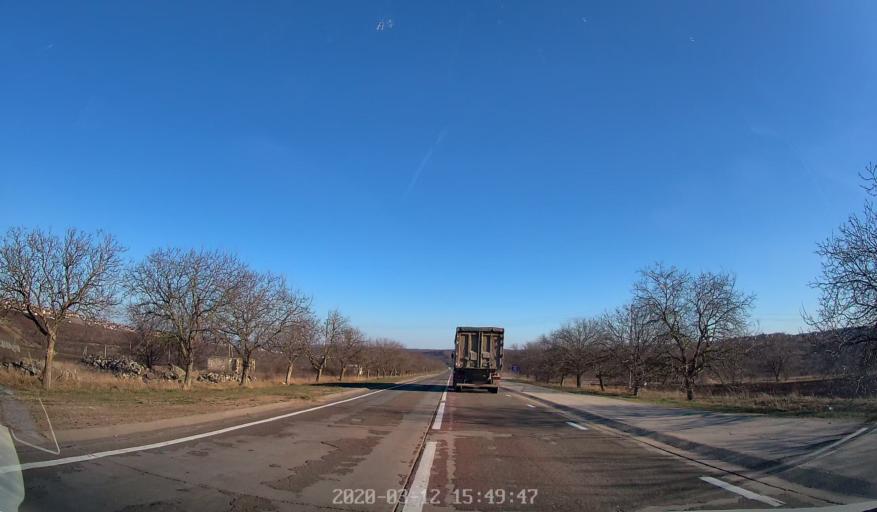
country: MD
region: Chisinau
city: Ciorescu
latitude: 47.0785
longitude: 28.9471
